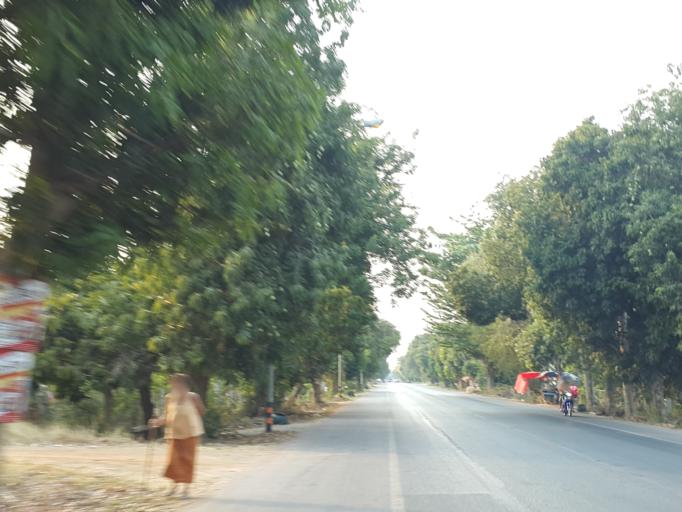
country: TH
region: Sukhothai
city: Si Samrong
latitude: 17.2173
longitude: 99.8637
